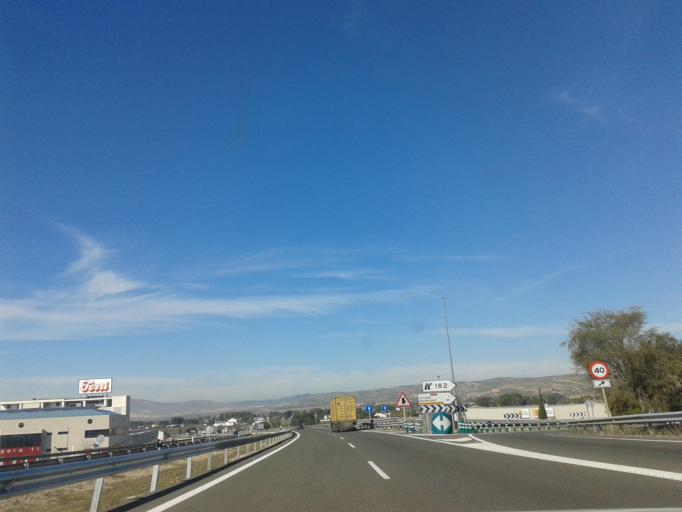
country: ES
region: Valencia
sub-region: Provincia de Alicante
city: Villena
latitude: 38.6448
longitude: -0.8658
